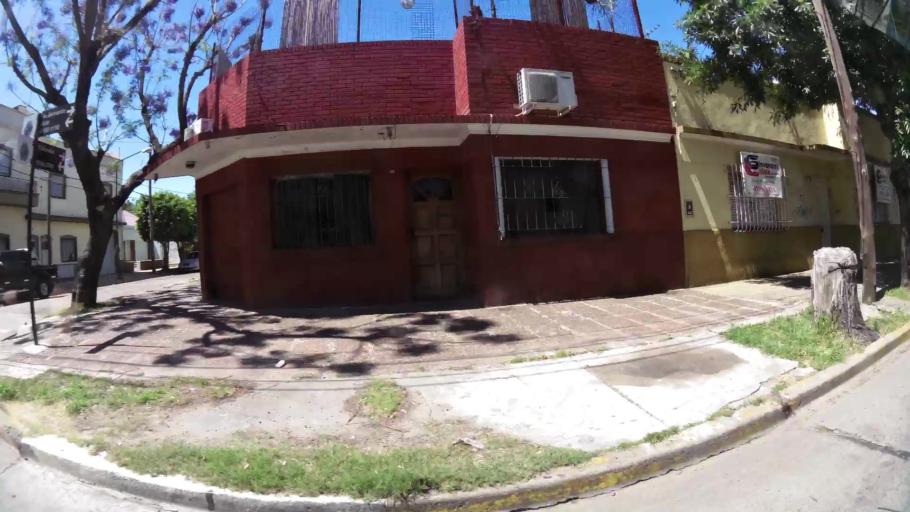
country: AR
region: Buenos Aires
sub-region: Partido de General San Martin
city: General San Martin
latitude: -34.5211
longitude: -58.5579
